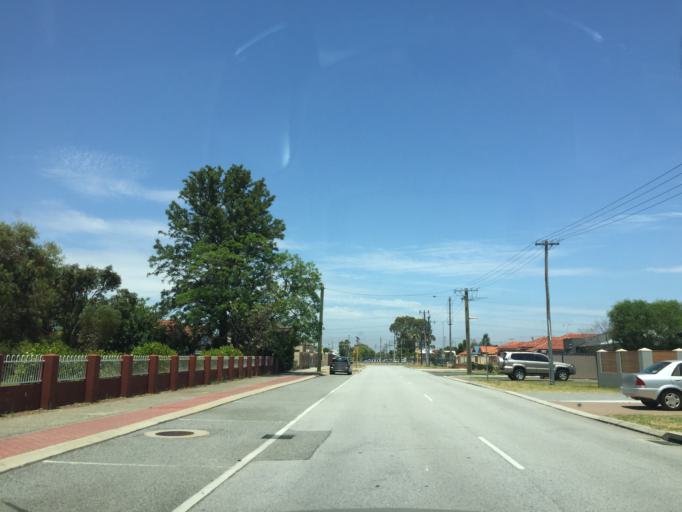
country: AU
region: Western Australia
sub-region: Canning
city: Queens Park
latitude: -32.0047
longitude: 115.9382
